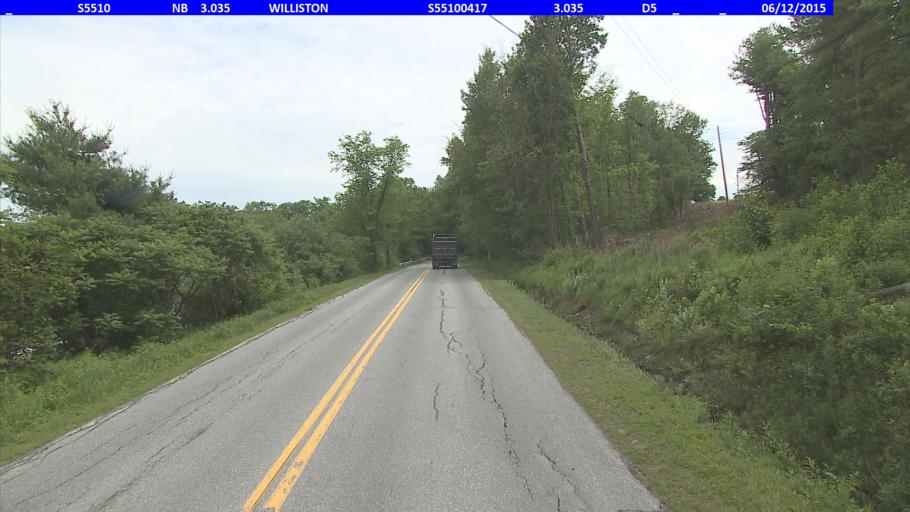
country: US
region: Vermont
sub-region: Chittenden County
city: Williston
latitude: 44.4152
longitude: -73.0867
